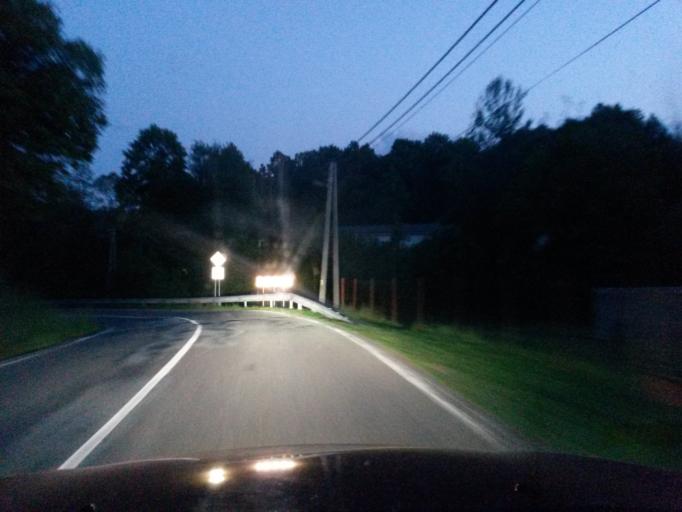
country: UA
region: Zakarpattia
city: Velykyi Bereznyi
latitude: 48.9224
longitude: 22.3178
